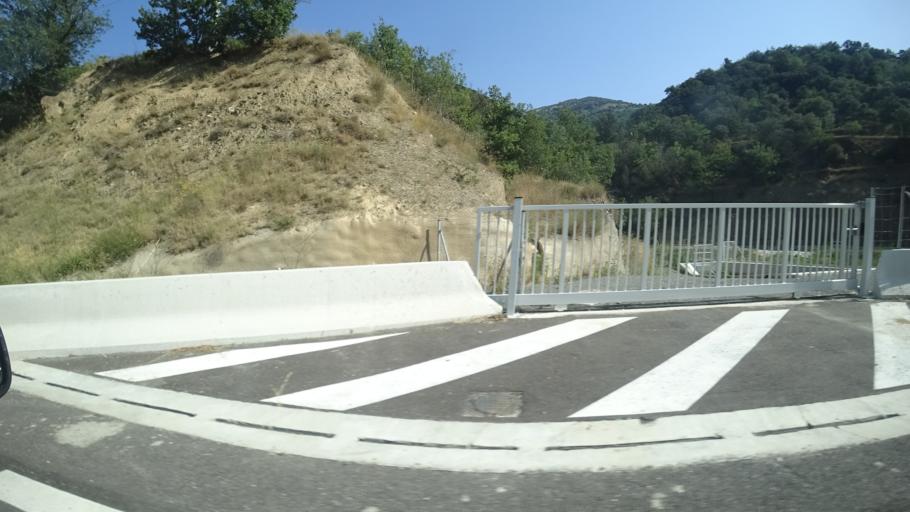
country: FR
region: Languedoc-Roussillon
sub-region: Departement des Pyrenees-Orientales
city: Vernet-les-Bains
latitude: 42.5612
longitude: 2.3004
